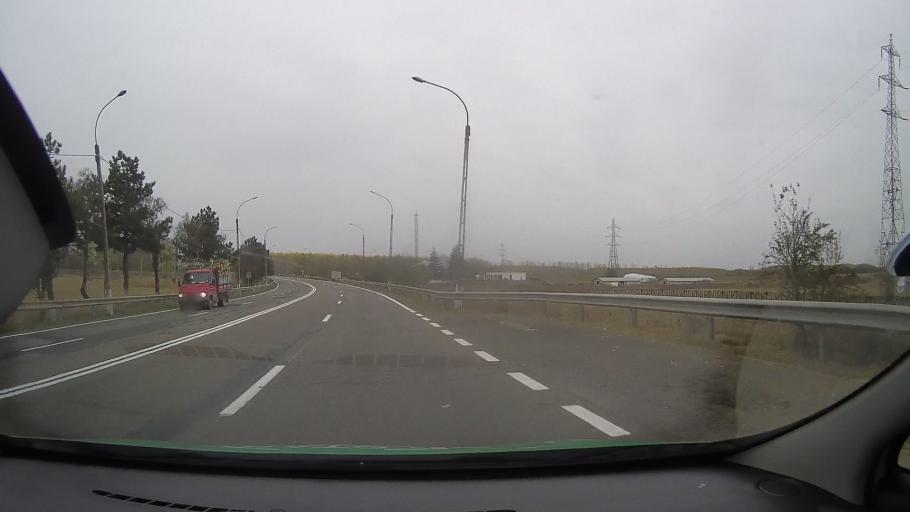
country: RO
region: Ialomita
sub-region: Comuna Giurgeni
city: Giurgeni
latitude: 44.7507
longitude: 27.8919
